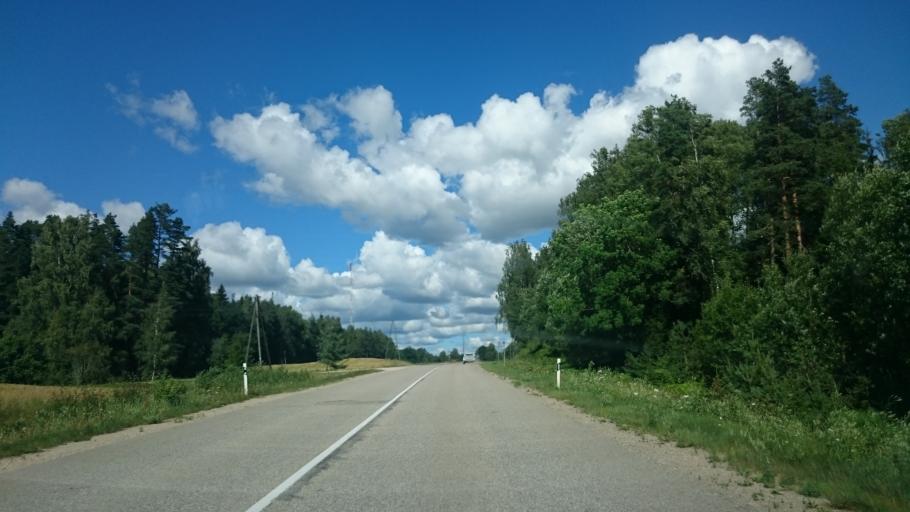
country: LV
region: Kuldigas Rajons
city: Kuldiga
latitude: 56.9240
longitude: 21.9114
